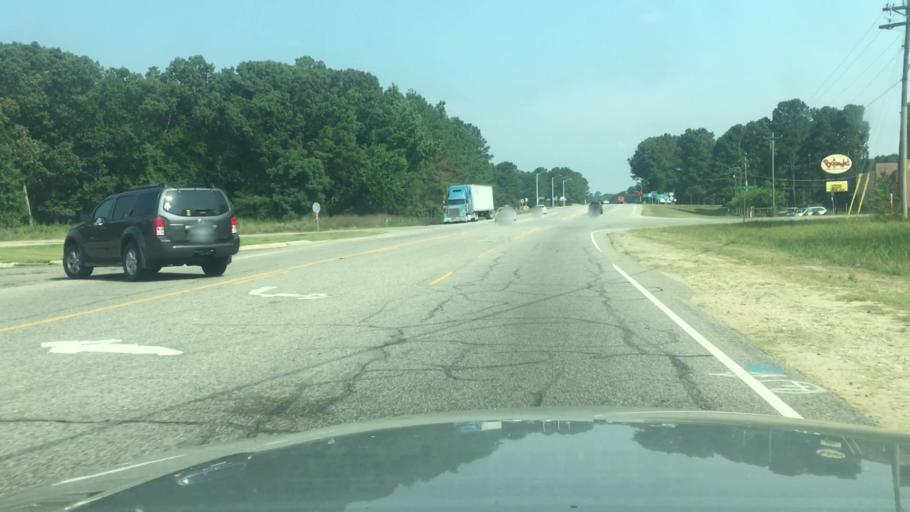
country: US
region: North Carolina
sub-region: Cumberland County
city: Hope Mills
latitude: 34.9354
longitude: -78.9208
